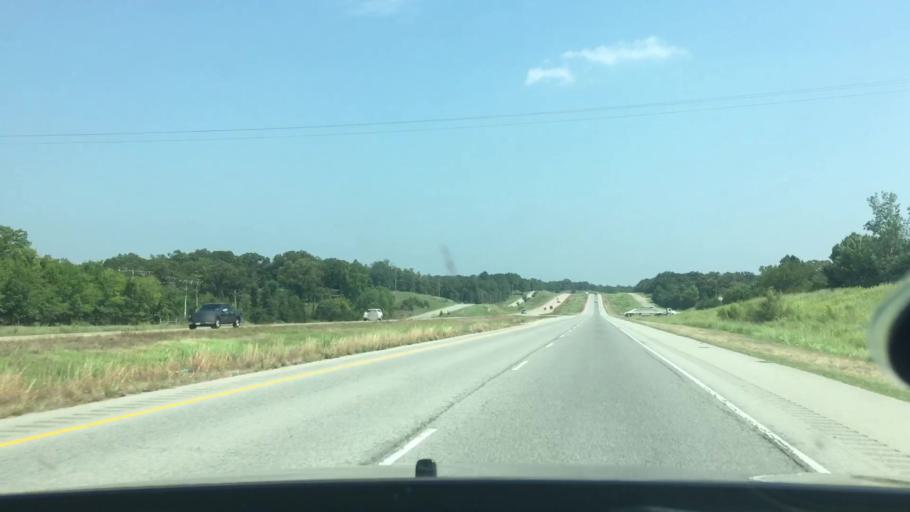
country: US
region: Oklahoma
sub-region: Atoka County
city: Atoka
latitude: 34.2860
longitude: -96.1970
